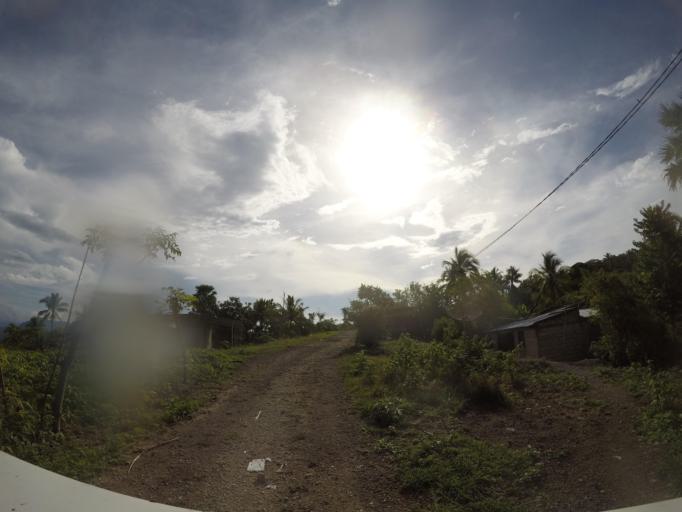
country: TL
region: Baucau
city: Baucau
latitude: -8.5044
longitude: 126.4497
